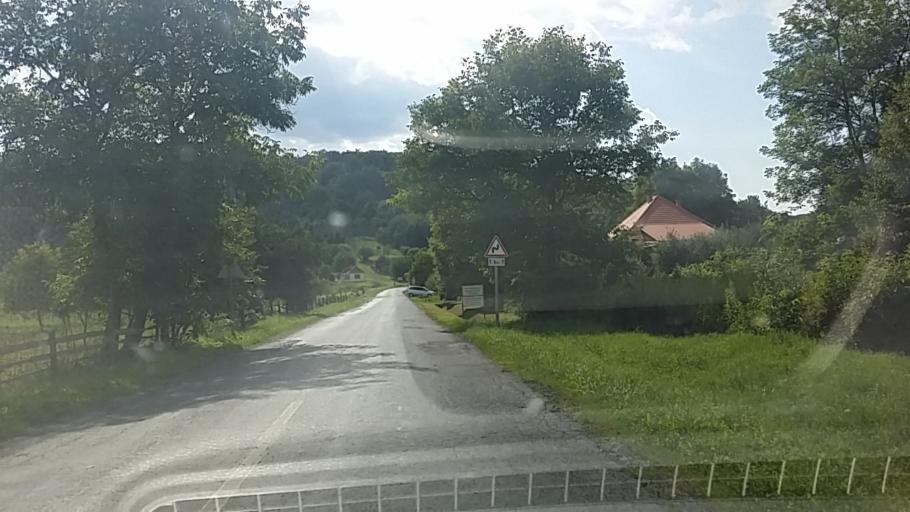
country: HU
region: Zala
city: Becsehely
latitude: 46.5253
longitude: 16.7588
